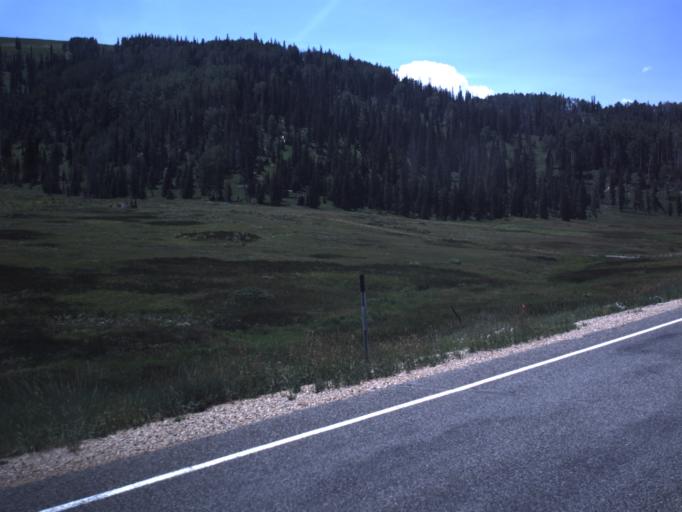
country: US
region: Utah
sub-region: Sanpete County
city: Fairview
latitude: 39.6490
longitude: -111.2692
